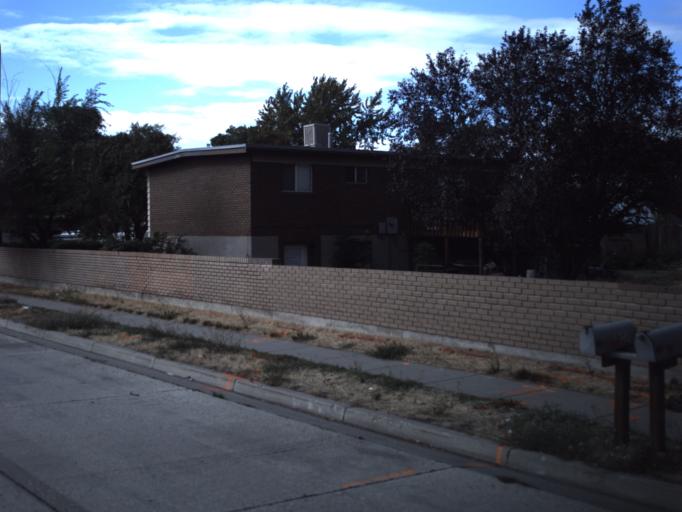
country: US
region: Utah
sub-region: Salt Lake County
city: Salt Lake City
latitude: 40.7766
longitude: -111.9394
